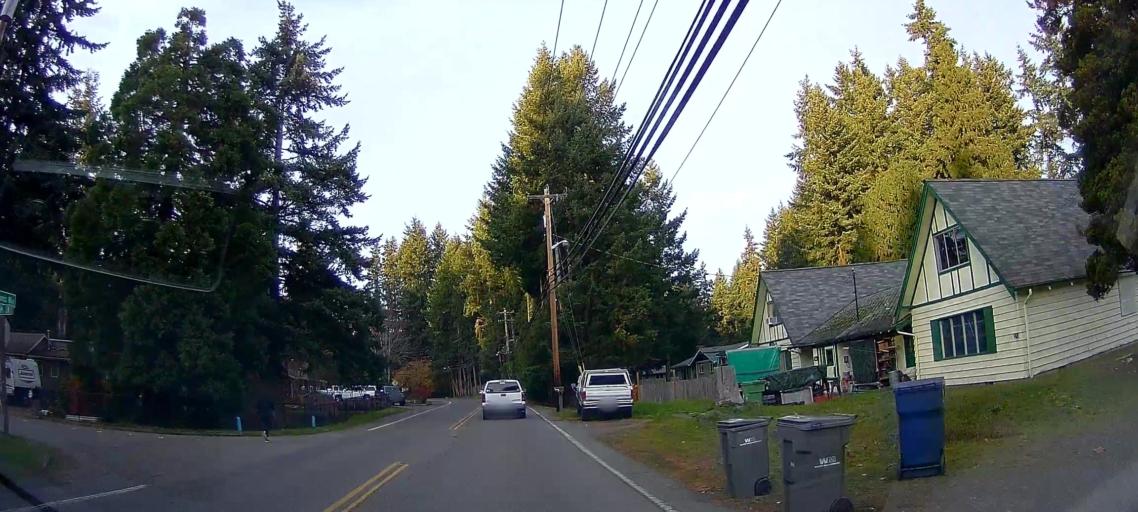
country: US
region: Washington
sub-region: Snohomish County
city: Alderwood Manor
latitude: 47.8154
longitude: -122.2575
